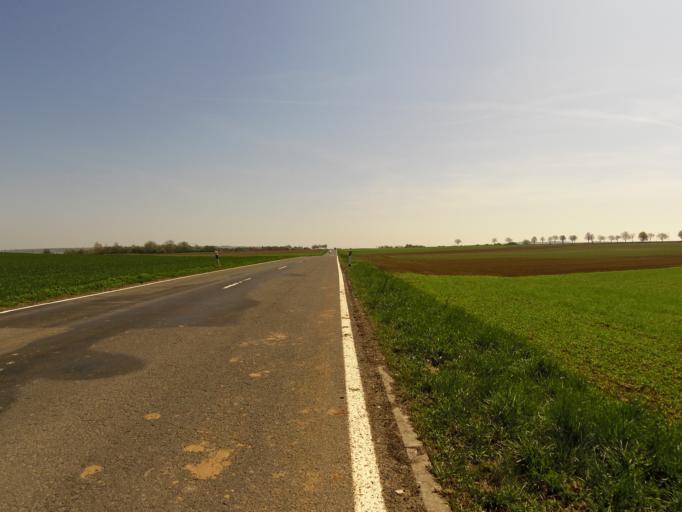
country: DE
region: Rheinland-Pfalz
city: Lautersheim
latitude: 49.5894
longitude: 8.0803
